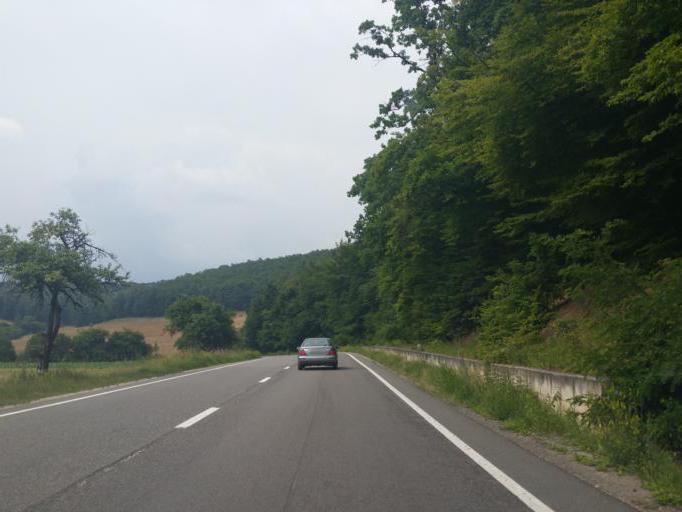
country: RO
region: Salaj
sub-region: Comuna Romanasi
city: Romanasi
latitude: 47.1160
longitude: 23.1654
